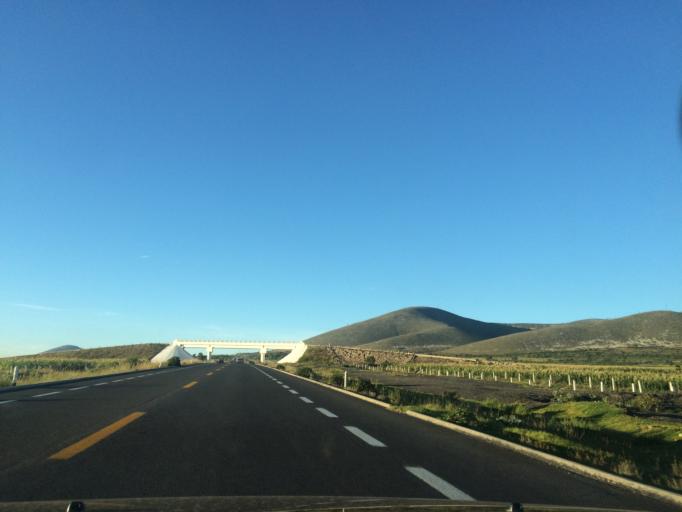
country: MX
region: Puebla
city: Morelos Canada
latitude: 18.7428
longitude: -97.4781
